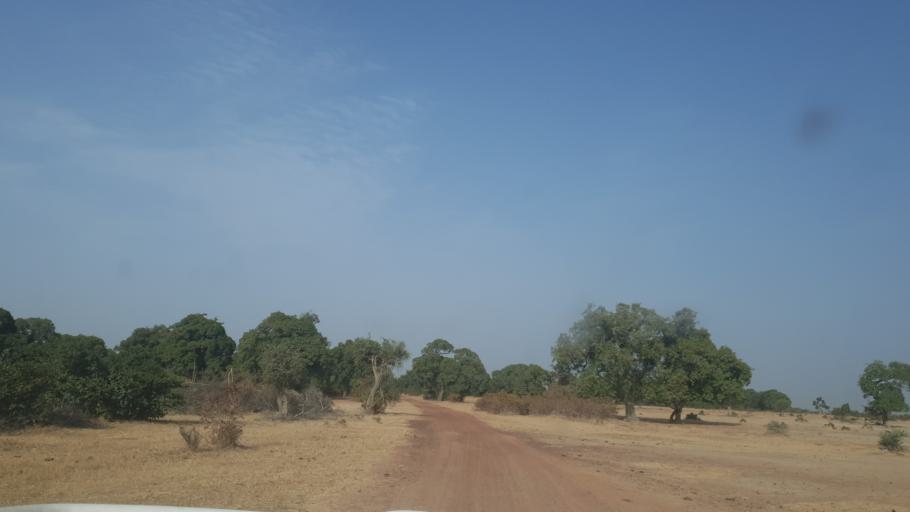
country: ML
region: Segou
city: Baroueli
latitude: 13.3584
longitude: -6.9239
